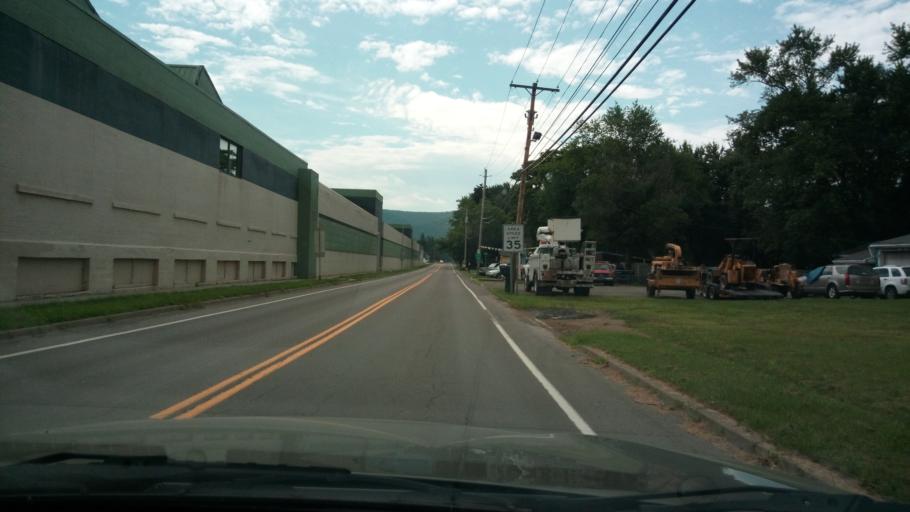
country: US
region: New York
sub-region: Chemung County
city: Elmira
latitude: 42.0673
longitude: -76.7973
